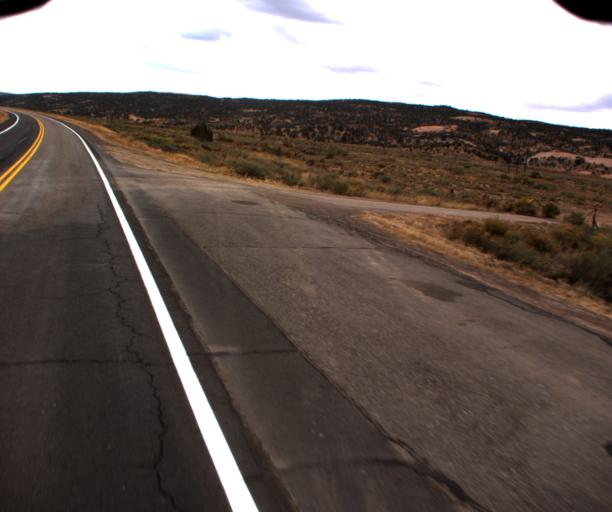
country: US
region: Arizona
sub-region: Navajo County
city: Kayenta
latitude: 36.6111
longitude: -110.4723
